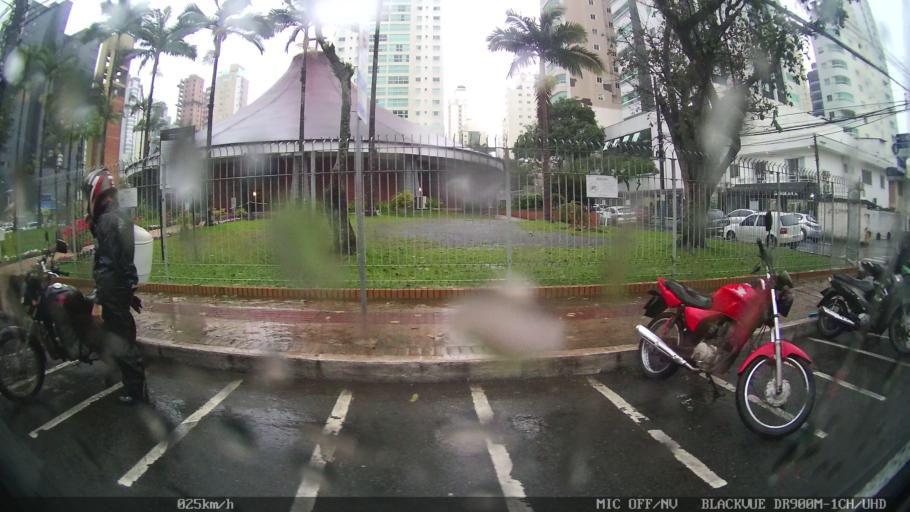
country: BR
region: Santa Catarina
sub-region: Balneario Camboriu
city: Balneario Camboriu
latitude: -26.9907
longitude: -48.6342
